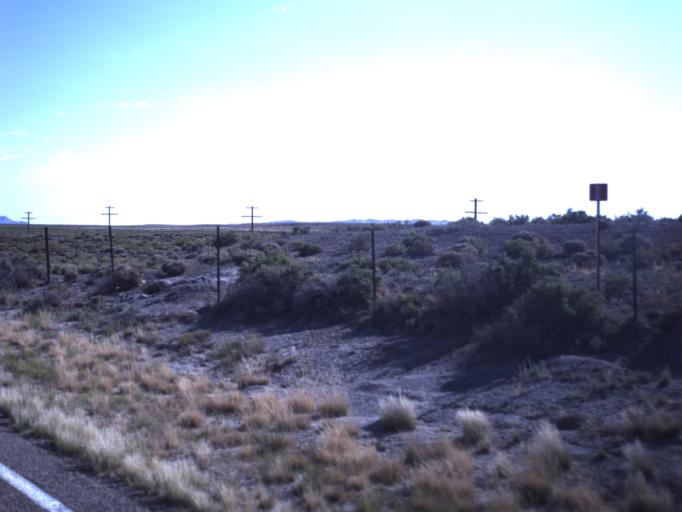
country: US
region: Utah
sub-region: Beaver County
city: Milford
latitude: 38.6251
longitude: -112.9847
